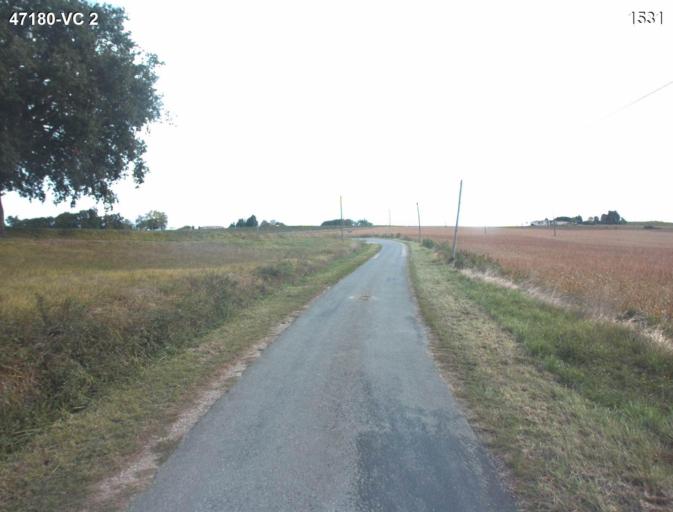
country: FR
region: Aquitaine
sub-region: Departement du Lot-et-Garonne
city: Sainte-Colombe-en-Bruilhois
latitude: 44.1689
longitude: 0.4360
